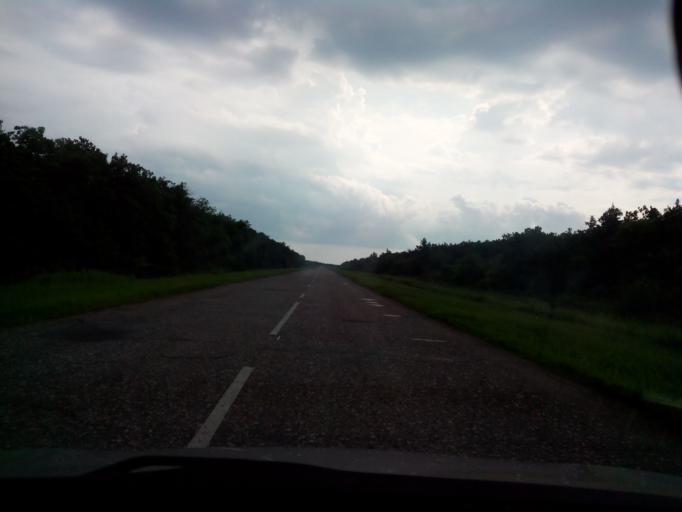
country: RU
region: Volgograd
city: Kumylzhenskaya
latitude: 49.9063
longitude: 42.8533
